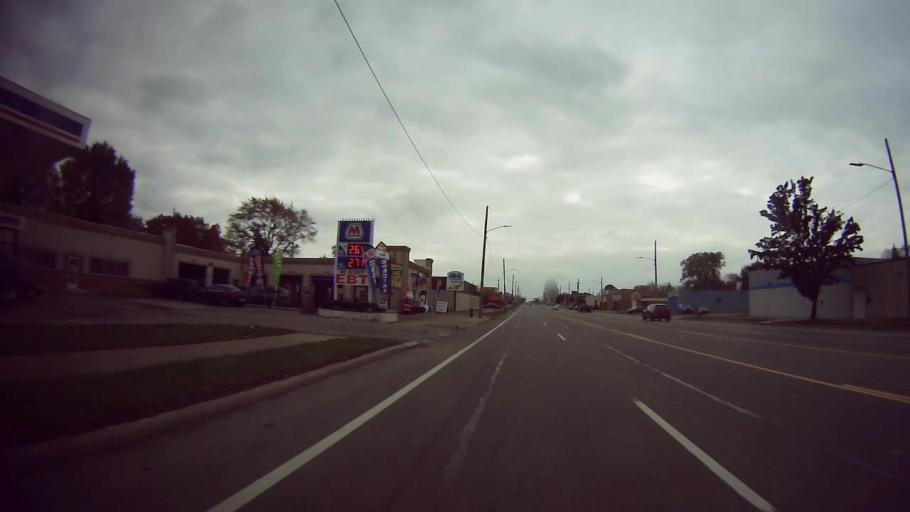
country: US
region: Michigan
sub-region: Macomb County
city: Warren
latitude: 42.4454
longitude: -83.0245
